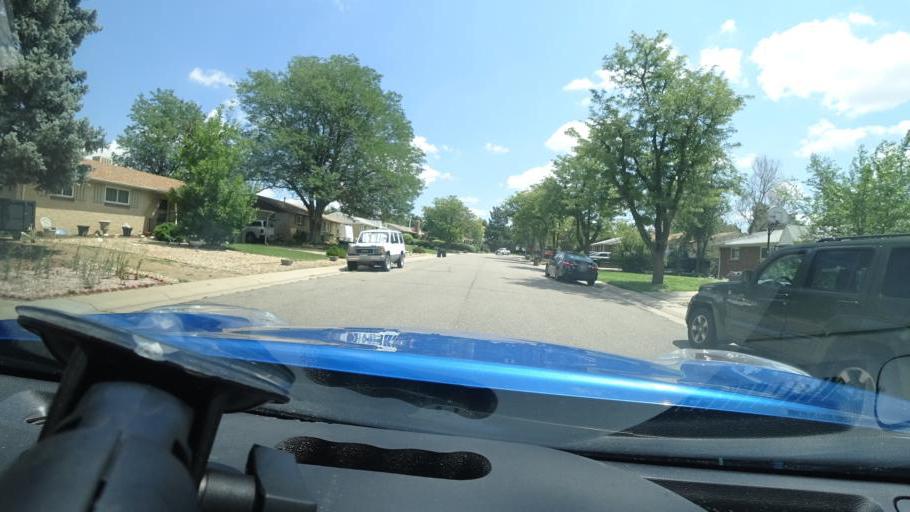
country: US
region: Colorado
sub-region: Adams County
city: Aurora
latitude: 39.7076
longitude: -104.8460
